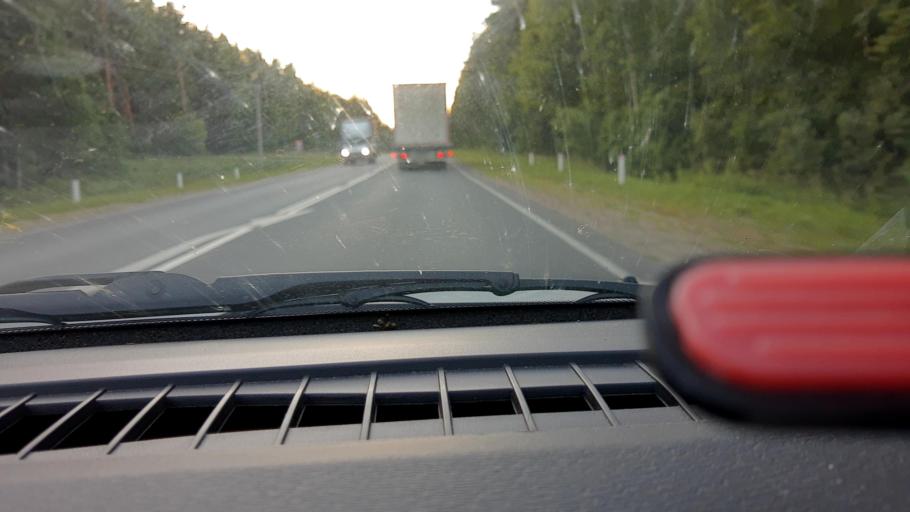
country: RU
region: Nizjnij Novgorod
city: Uren'
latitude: 57.3537
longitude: 45.7029
